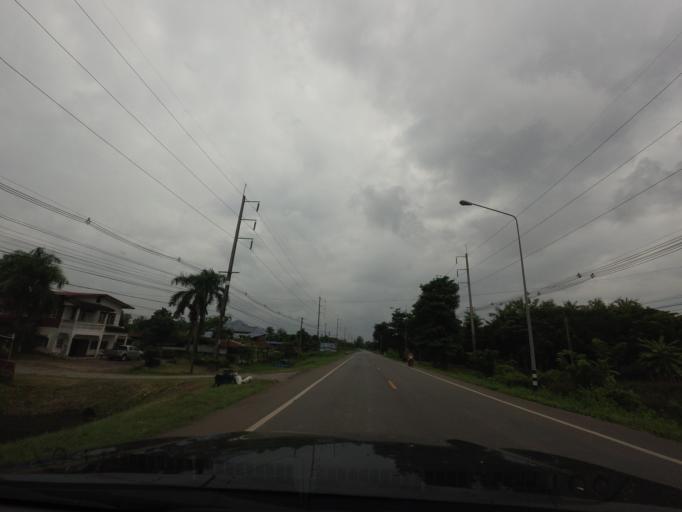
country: TH
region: Nong Khai
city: Tha Bo
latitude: 17.9007
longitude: 102.6044
